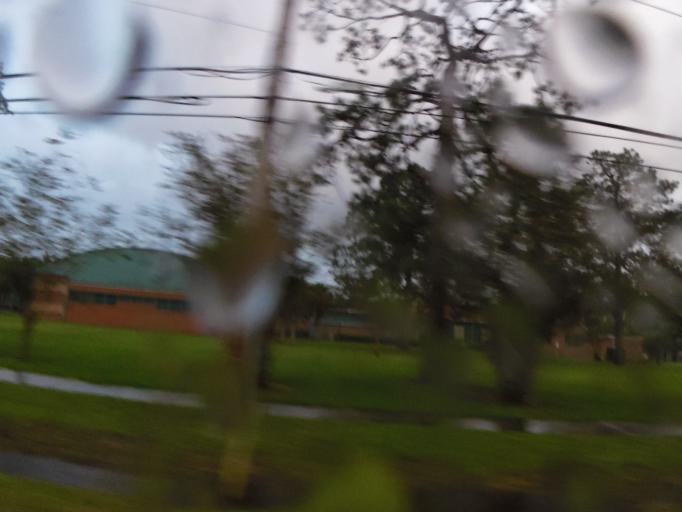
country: US
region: Florida
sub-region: Duval County
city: Jacksonville
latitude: 30.3141
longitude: -81.7426
